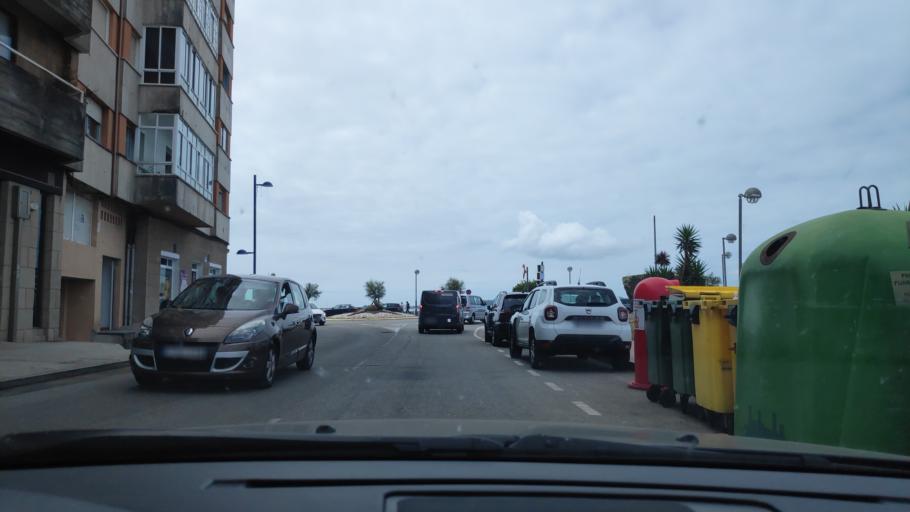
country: ES
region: Galicia
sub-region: Provincia de Pontevedra
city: Cambados
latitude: 42.5194
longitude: -8.8169
